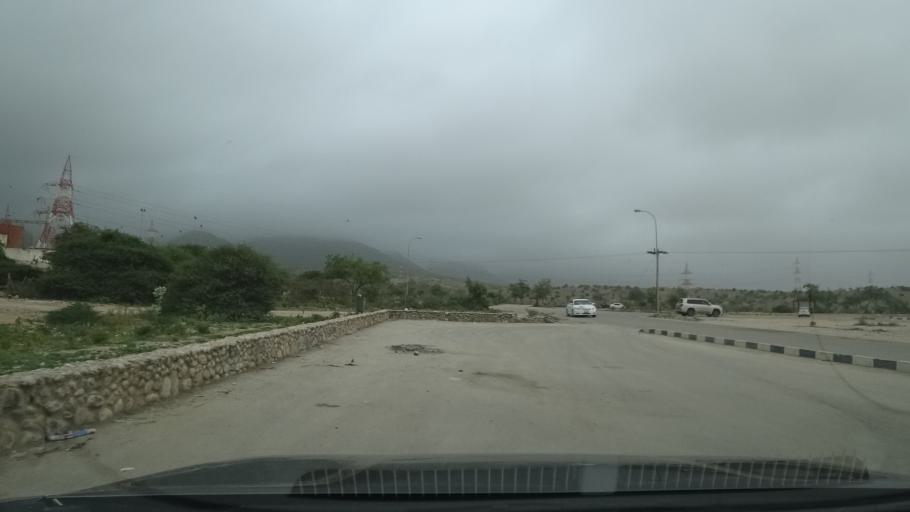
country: OM
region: Zufar
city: Salalah
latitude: 17.0900
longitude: 54.0784
